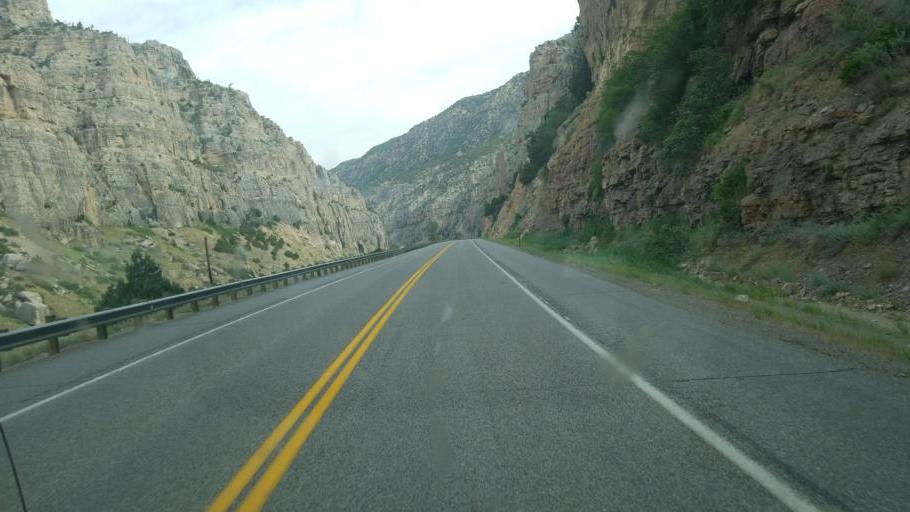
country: US
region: Wyoming
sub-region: Hot Springs County
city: Thermopolis
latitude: 43.5309
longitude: -108.1782
